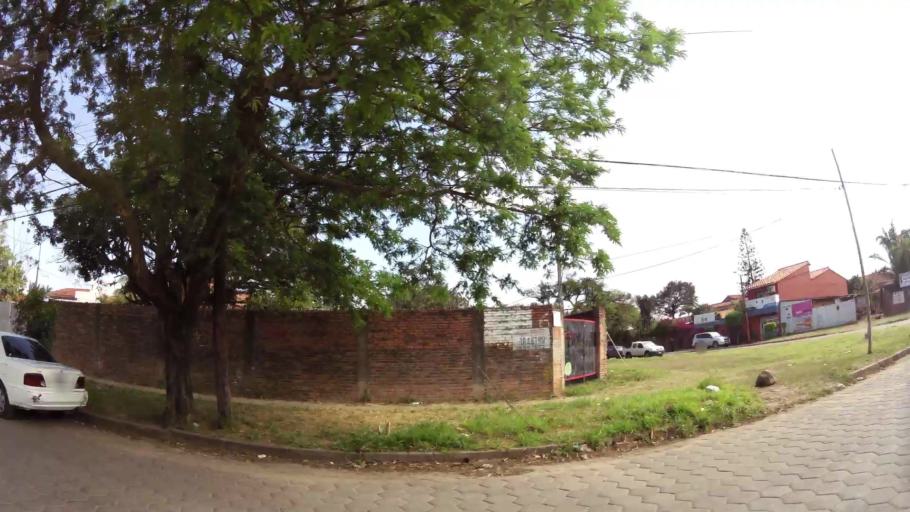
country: BO
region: Santa Cruz
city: Santa Cruz de la Sierra
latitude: -17.7490
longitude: -63.1565
